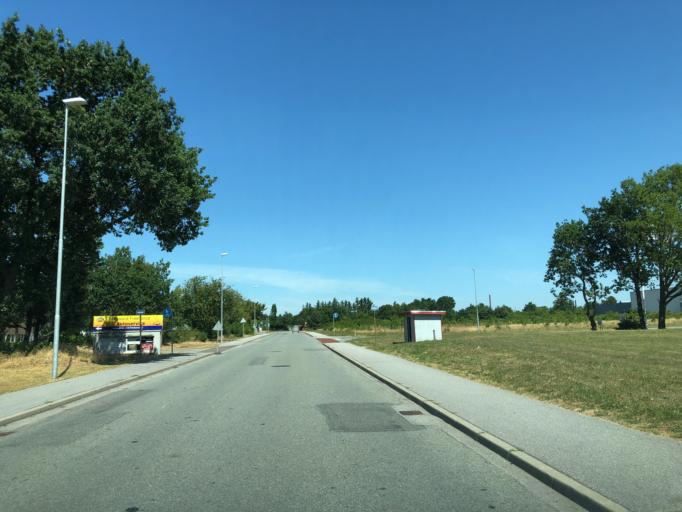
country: DK
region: Central Jutland
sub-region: Skive Kommune
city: Skive
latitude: 56.5410
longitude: 9.0298
